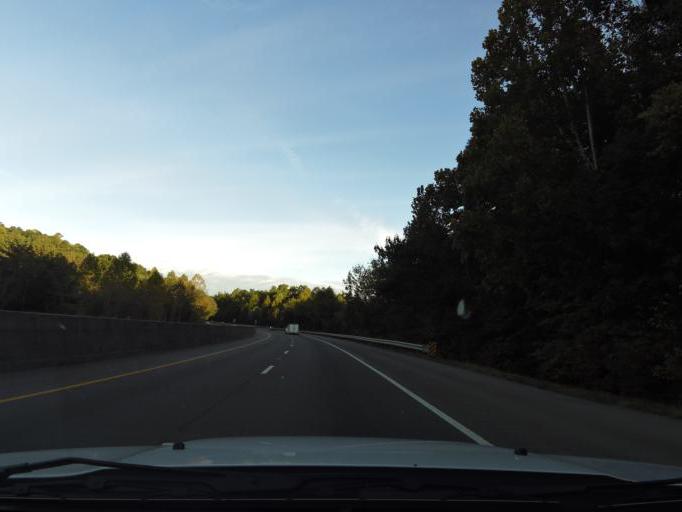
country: US
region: Tennessee
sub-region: Anderson County
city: Norris
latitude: 36.1134
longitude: -84.0254
